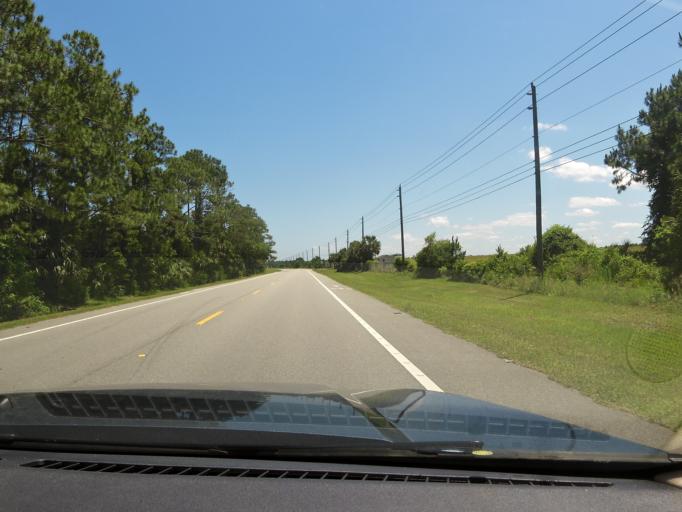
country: US
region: Florida
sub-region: Flagler County
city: Flagler Beach
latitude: 29.4623
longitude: -81.1714
